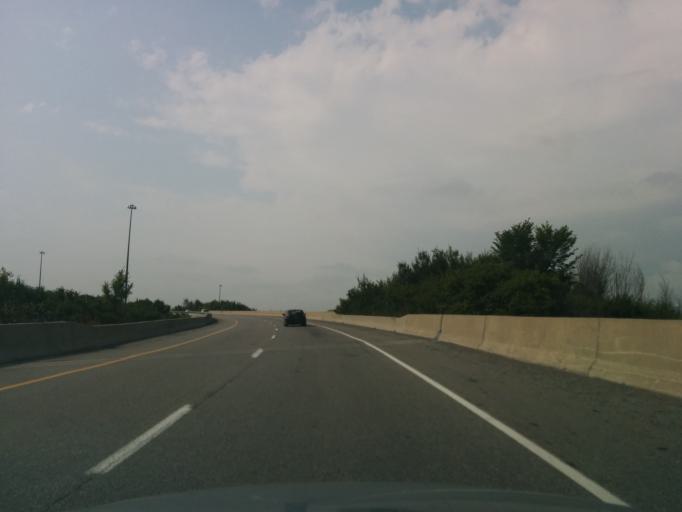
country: CA
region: Ontario
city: Bells Corners
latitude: 45.3442
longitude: -75.8131
